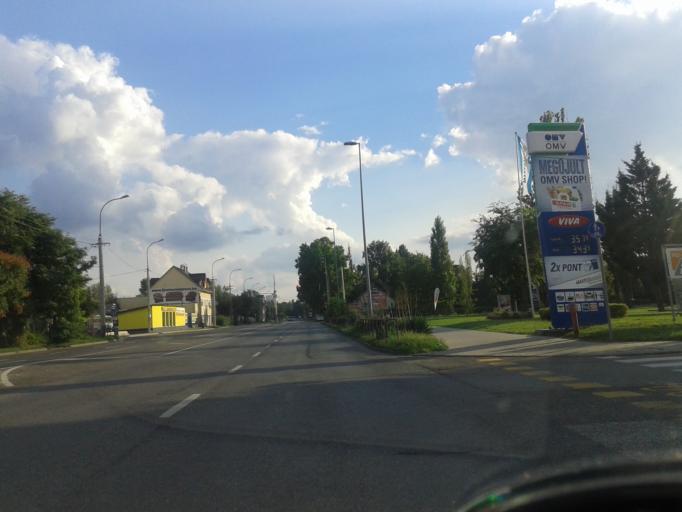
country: HU
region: Budapest
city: Budapest XXI. keruelet
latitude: 47.4139
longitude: 19.0589
